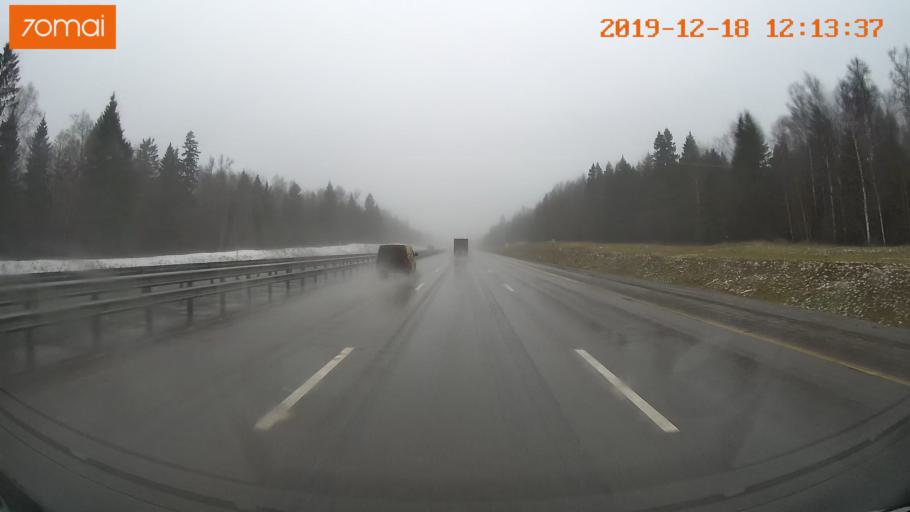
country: RU
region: Moskovskaya
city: Rumyantsevo
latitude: 55.9511
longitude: 36.5240
